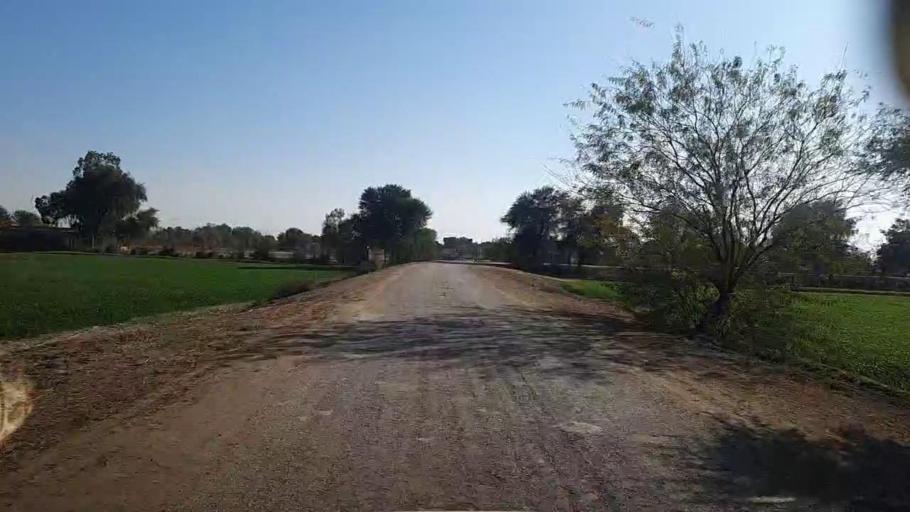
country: PK
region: Sindh
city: Khairpur
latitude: 27.9149
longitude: 69.7519
